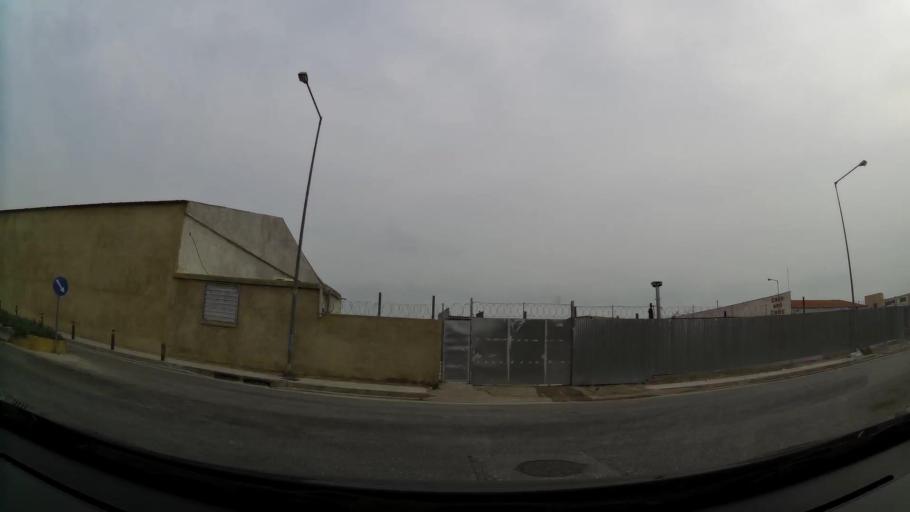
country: GR
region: Attica
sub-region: Nomarchia Athinas
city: Moskhaton
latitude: 37.9592
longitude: 23.6793
